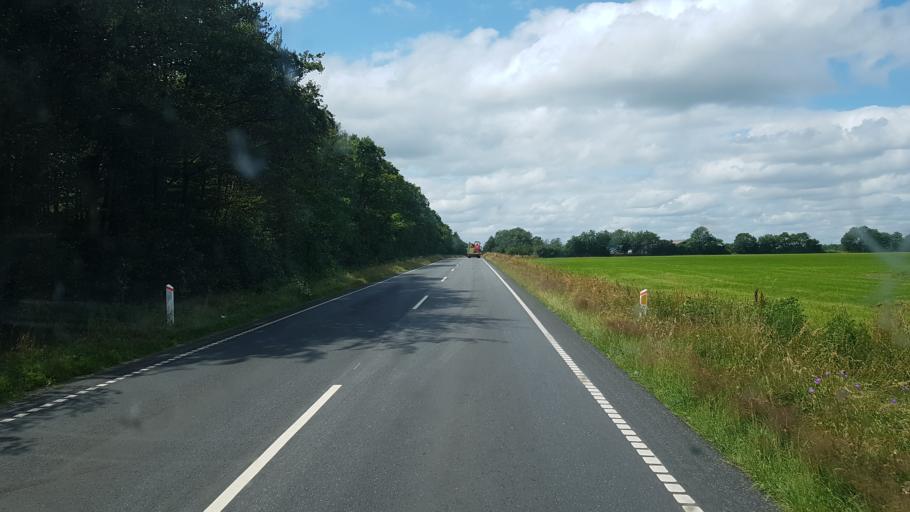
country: DK
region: South Denmark
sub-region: Vejen Kommune
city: Holsted
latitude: 55.5142
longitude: 8.8642
